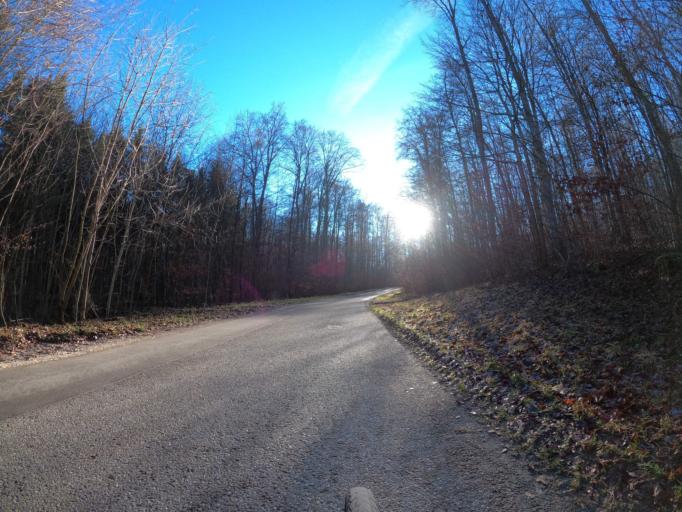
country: DE
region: Baden-Wuerttemberg
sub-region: Tuebingen Region
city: Sankt Johann
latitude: 48.4381
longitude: 9.2965
